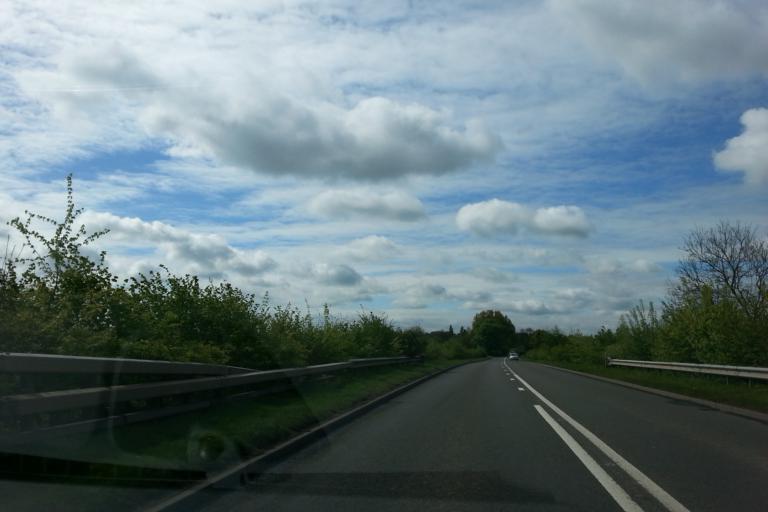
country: GB
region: England
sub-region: Staffordshire
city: Lichfield
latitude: 52.7193
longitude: -1.8417
